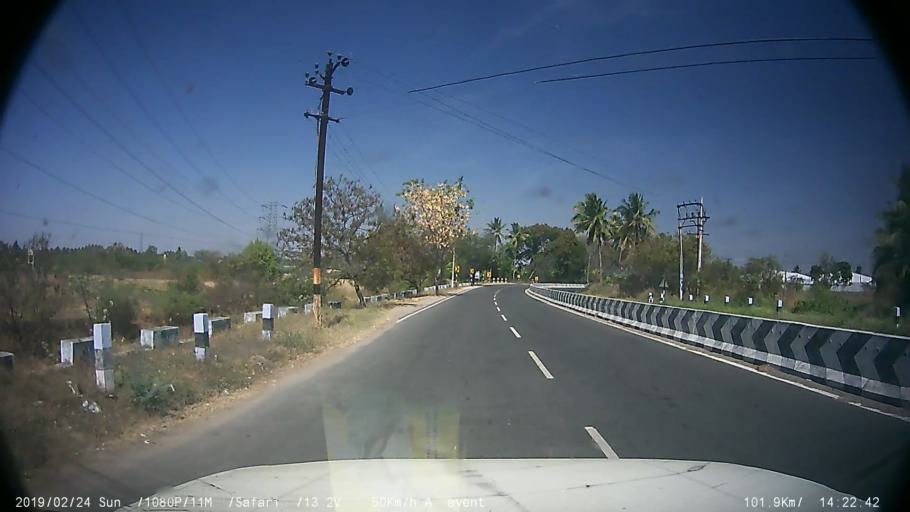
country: IN
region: Tamil Nadu
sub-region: Tiruppur
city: Avinashi
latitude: 11.2015
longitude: 77.2349
